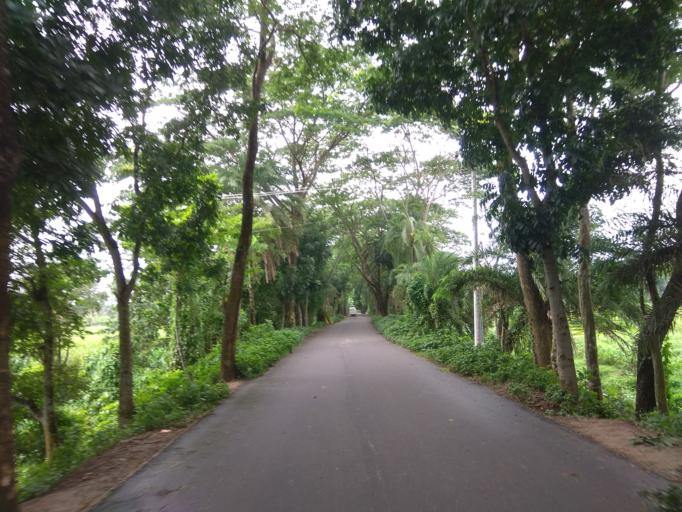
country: BD
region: Dhaka
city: Dohar
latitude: 23.4284
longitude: 90.0682
